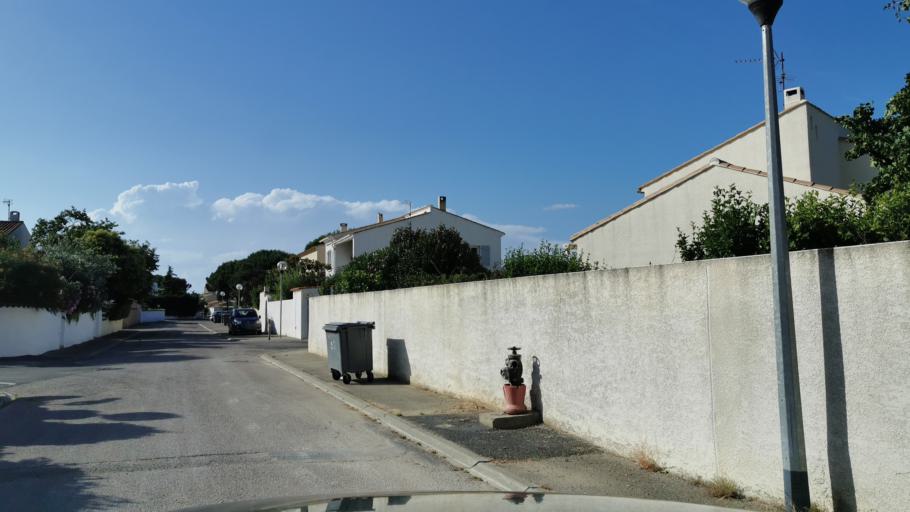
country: FR
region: Languedoc-Roussillon
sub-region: Departement de l'Aude
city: Narbonne
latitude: 43.1731
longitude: 3.0101
